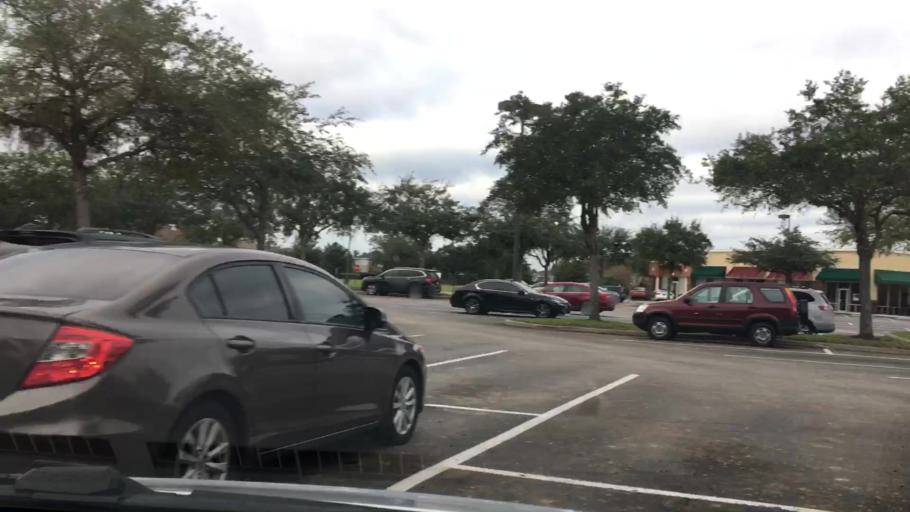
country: US
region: Florida
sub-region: Orange County
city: Conway
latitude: 28.4703
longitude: -81.2668
